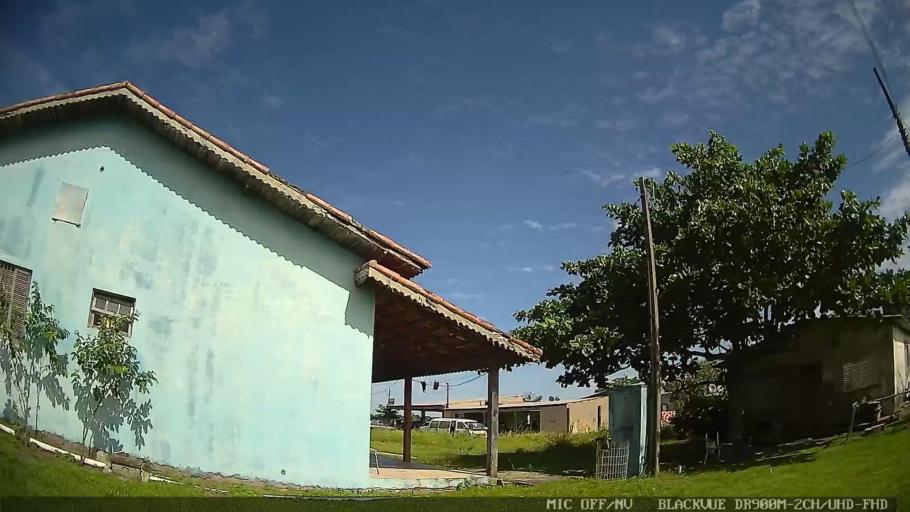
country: BR
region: Sao Paulo
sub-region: Iguape
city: Iguape
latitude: -24.7774
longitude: -47.5976
